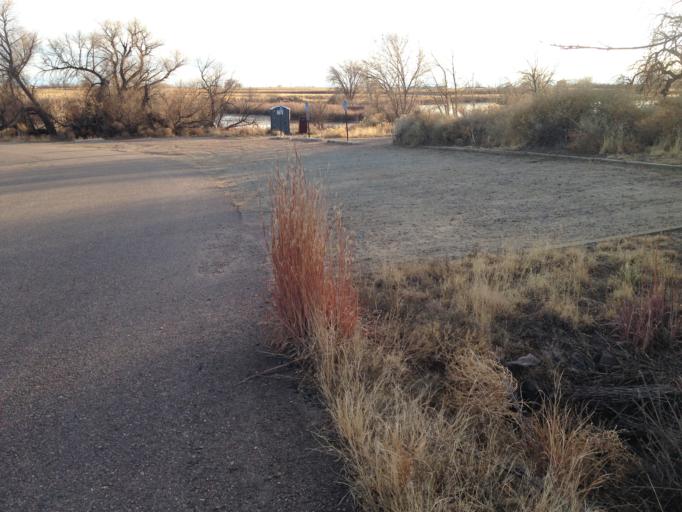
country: US
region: Colorado
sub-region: Adams County
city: Derby
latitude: 39.8204
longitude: -104.8625
